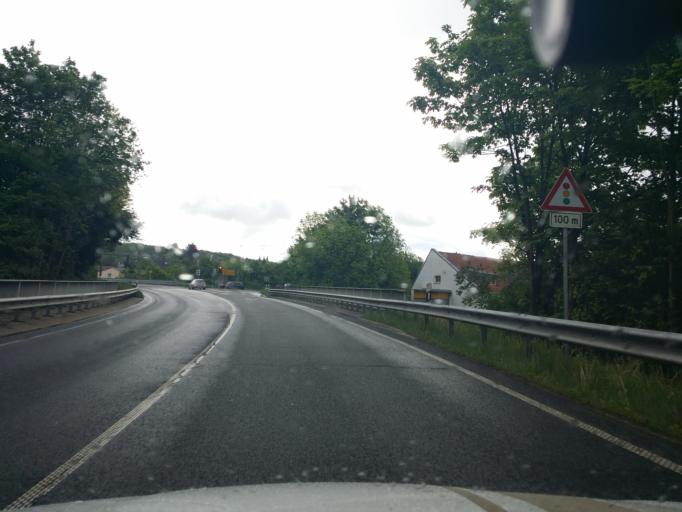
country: DE
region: Hesse
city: Eppstein
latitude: 50.1506
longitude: 8.4213
